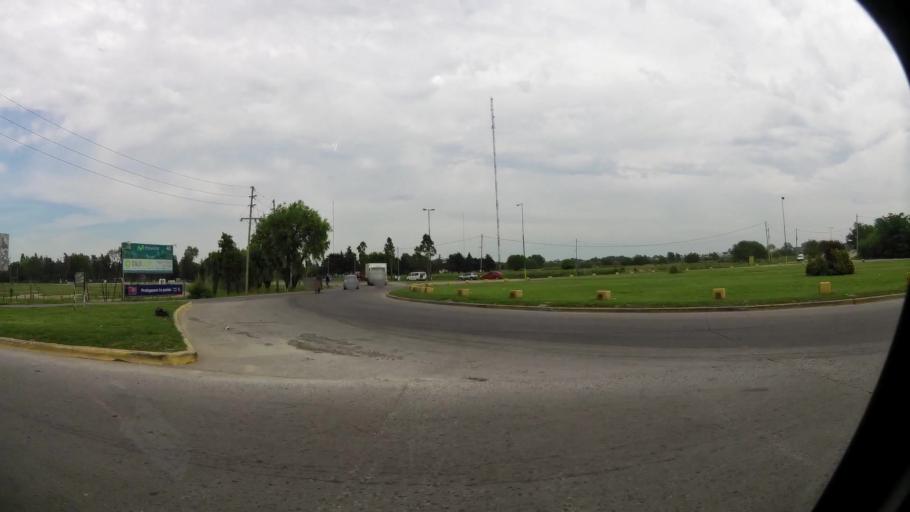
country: AR
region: Buenos Aires
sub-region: Partido de La Plata
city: La Plata
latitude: -34.9073
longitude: -58.0007
